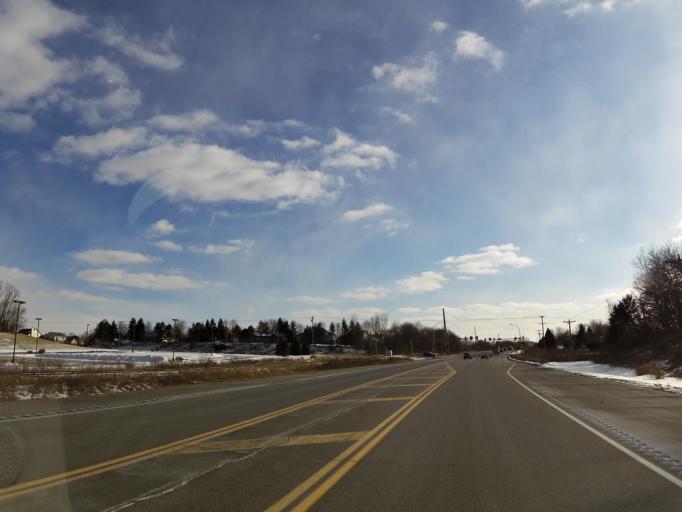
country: US
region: Minnesota
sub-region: Dakota County
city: Rosemount
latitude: 44.7918
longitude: -93.1085
